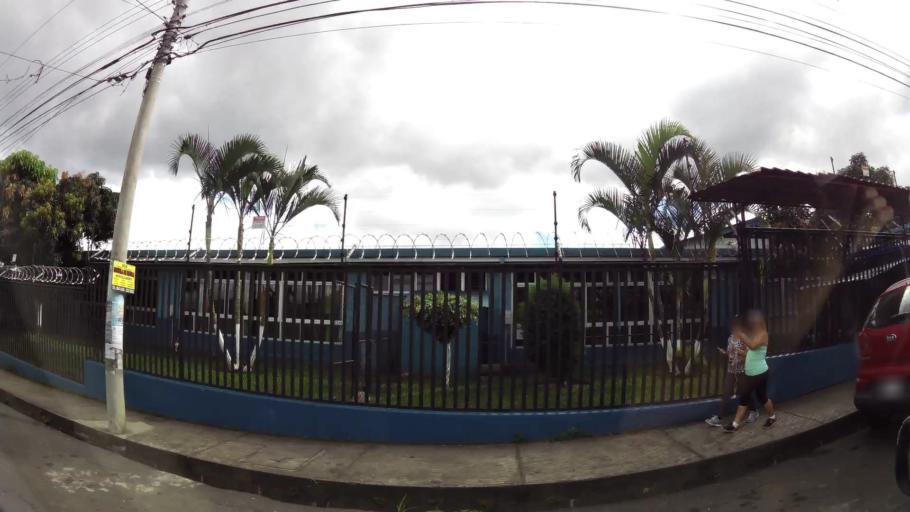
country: CR
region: San Jose
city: Alajuelita
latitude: 9.9007
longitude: -84.0999
